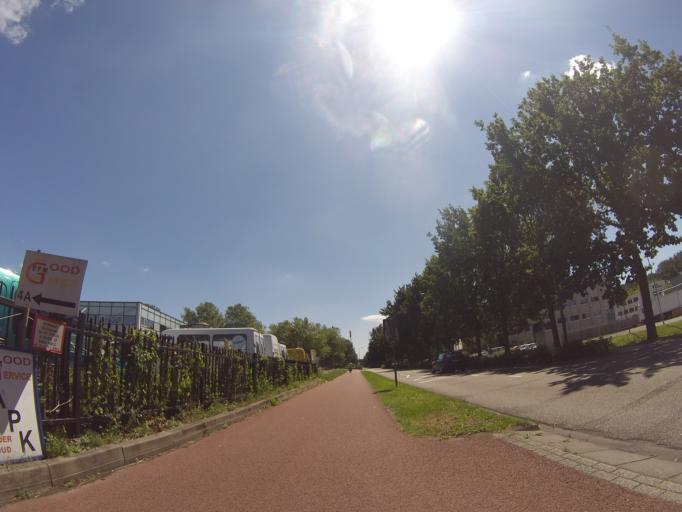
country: NL
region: Utrecht
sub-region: Stichtse Vecht
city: Maarssen
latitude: 52.1281
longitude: 5.0382
